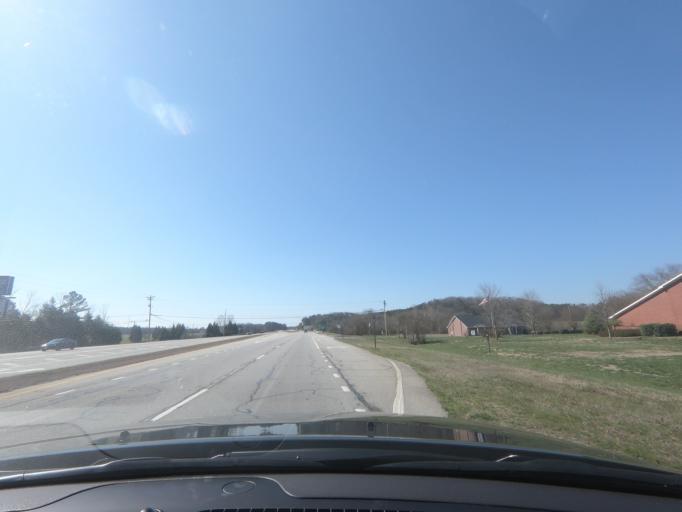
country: US
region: Georgia
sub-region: Gordon County
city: Calhoun
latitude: 34.4627
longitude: -84.9816
